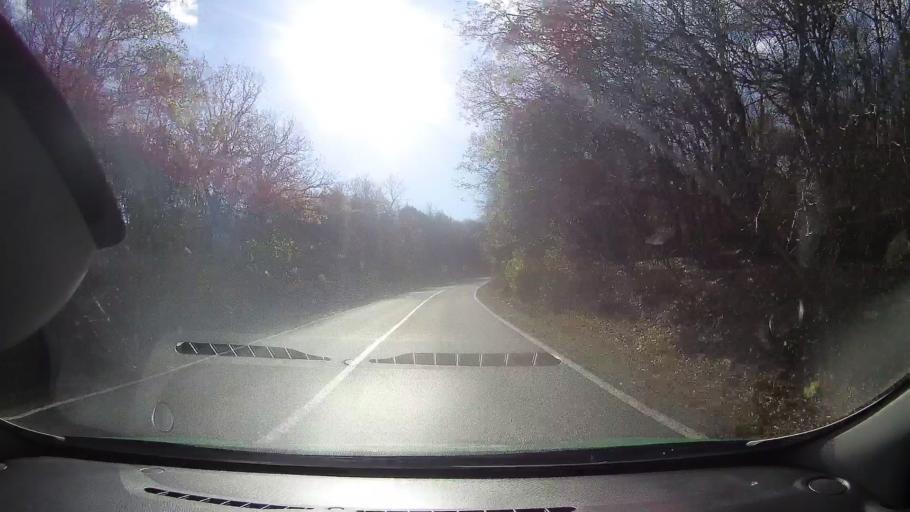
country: RO
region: Tulcea
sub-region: Oras Babadag
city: Babadag
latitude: 44.8430
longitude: 28.6975
